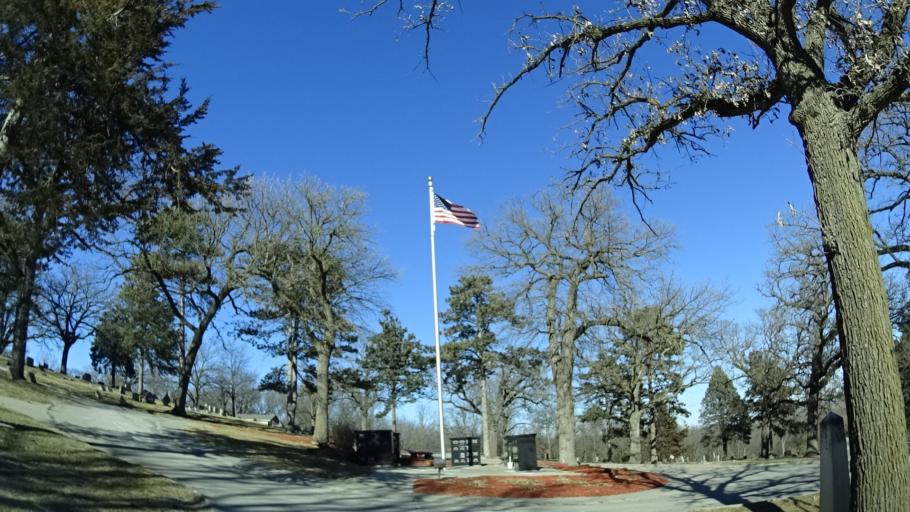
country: US
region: Nebraska
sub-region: Sarpy County
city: Bellevue
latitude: 41.1491
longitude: -95.8947
